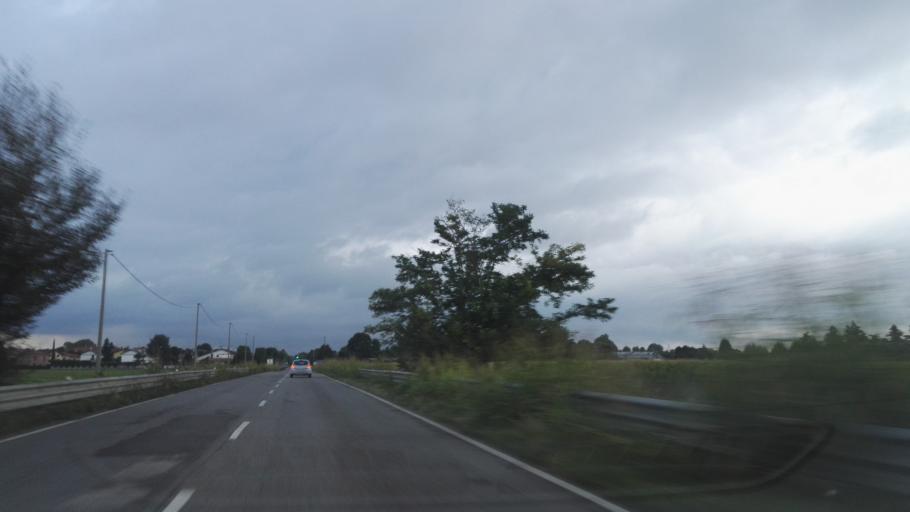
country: IT
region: Lombardy
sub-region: Citta metropolitana di Milano
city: Settala
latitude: 45.4485
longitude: 9.3922
